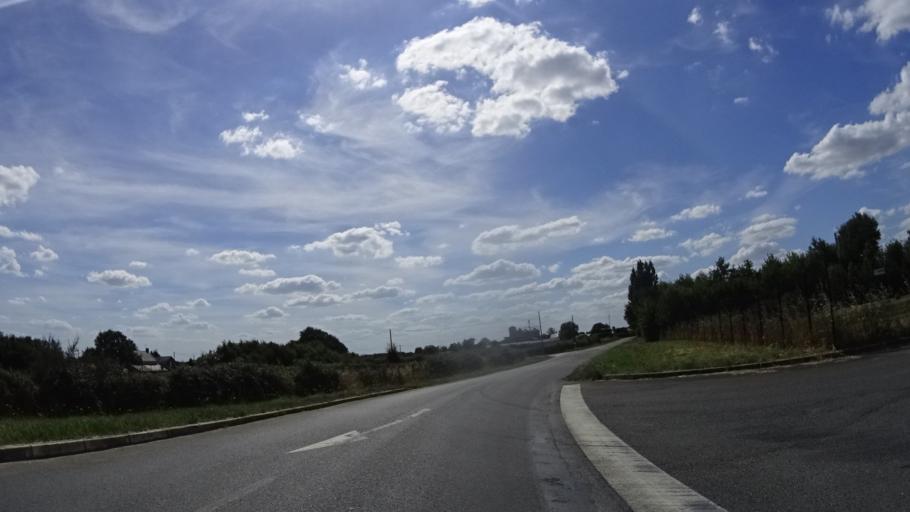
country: FR
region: Pays de la Loire
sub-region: Departement de la Loire-Atlantique
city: Saint-Mars-la-Jaille
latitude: 47.5727
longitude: -1.1913
